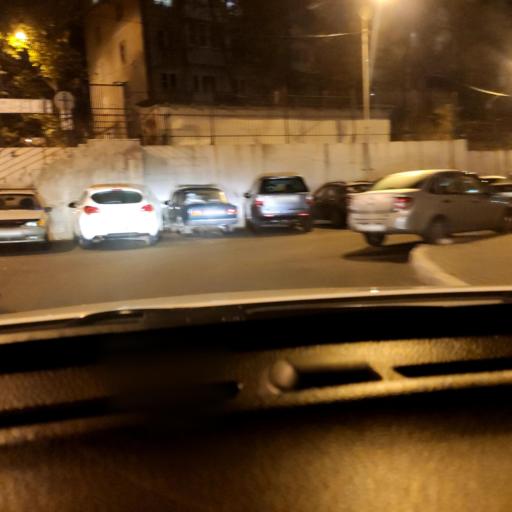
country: RU
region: Voronezj
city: Voronezh
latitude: 51.6982
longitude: 39.2217
